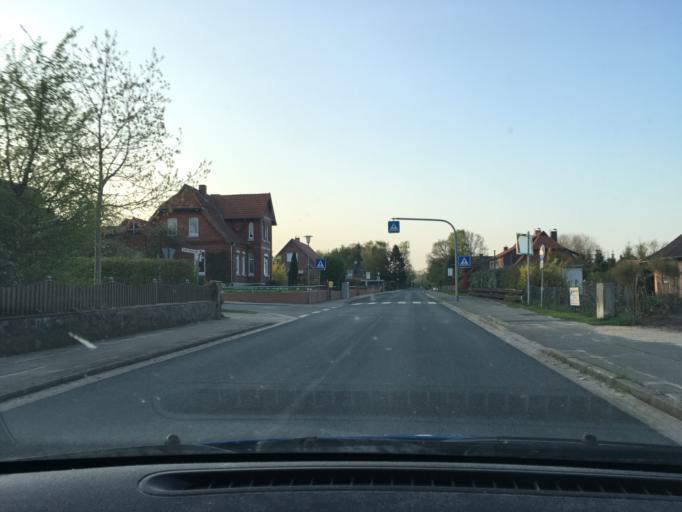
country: DE
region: Lower Saxony
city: Sudergellersen
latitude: 53.2125
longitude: 10.2976
